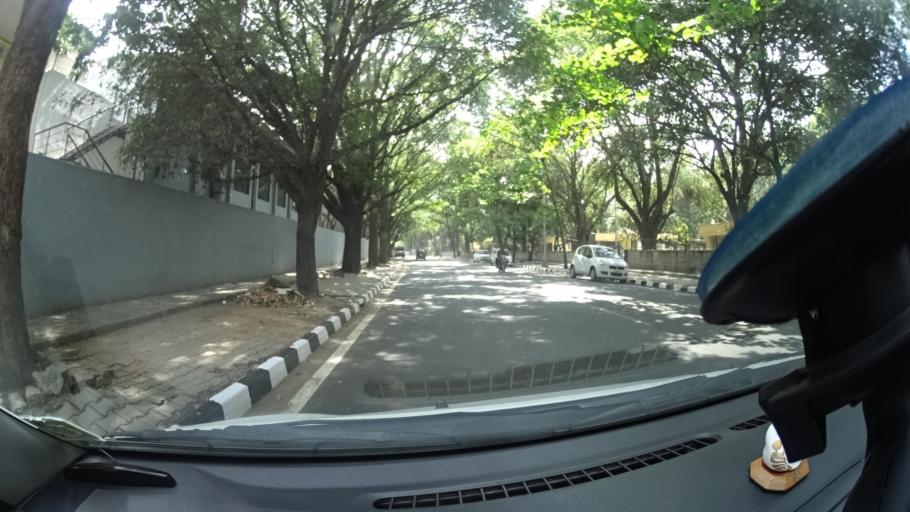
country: IN
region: Karnataka
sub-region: Bangalore Urban
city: Yelahanka
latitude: 13.1025
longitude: 77.5831
